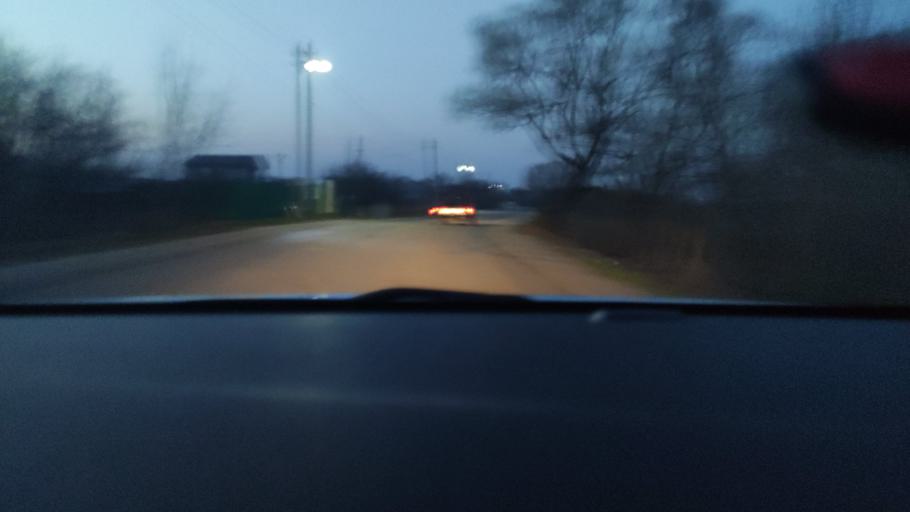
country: RU
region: Voronezj
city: Shilovo
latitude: 51.4735
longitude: 39.0222
